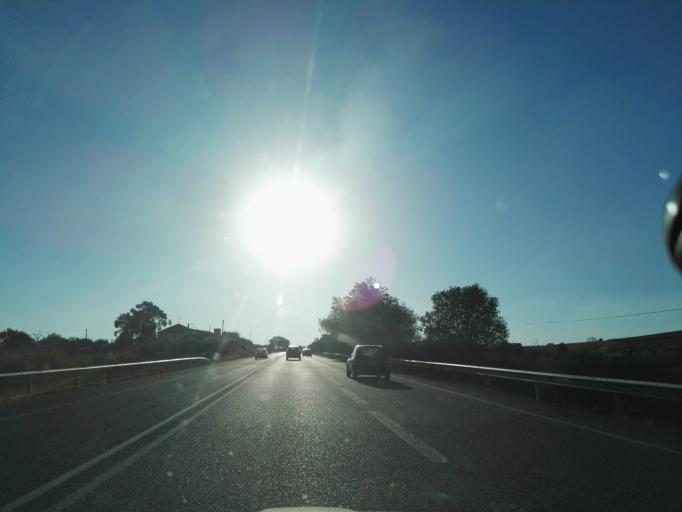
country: PT
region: Evora
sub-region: Borba
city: Borba
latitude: 38.8186
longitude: -7.4388
